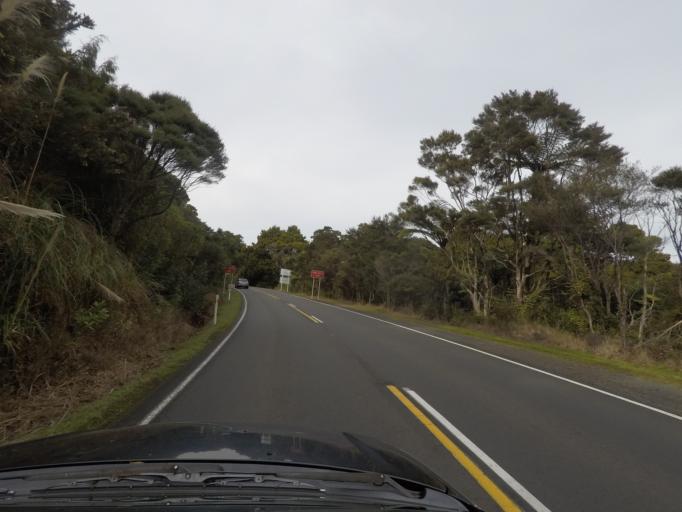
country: NZ
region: Auckland
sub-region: Auckland
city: Titirangi
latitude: -36.9332
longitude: 174.5721
